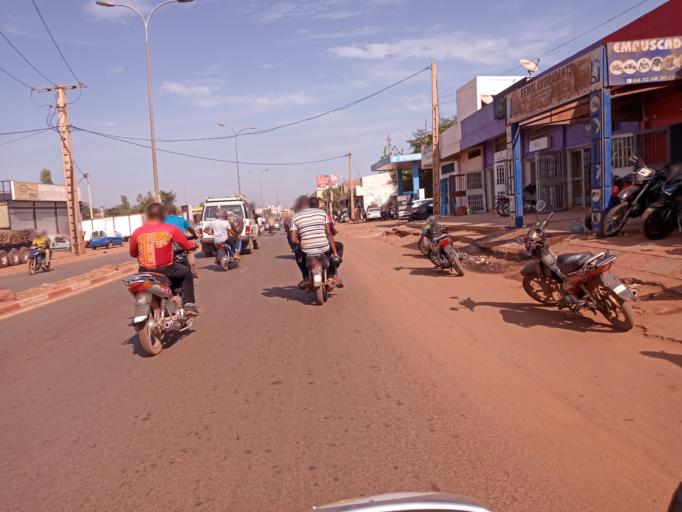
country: ML
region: Bamako
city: Bamako
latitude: 12.6658
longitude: -7.9333
